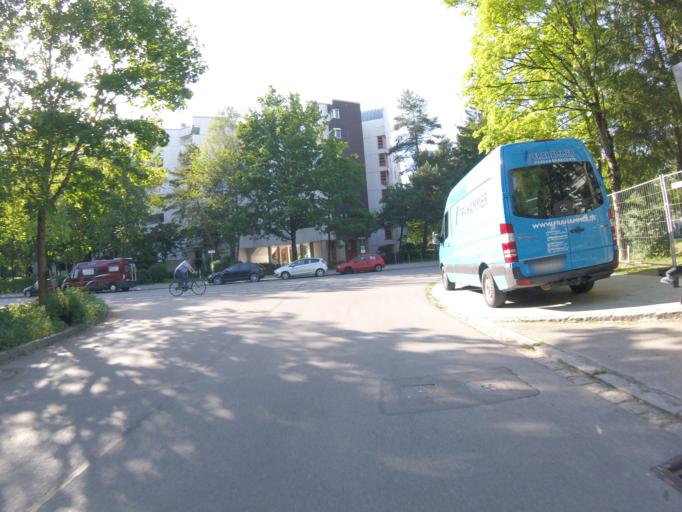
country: DE
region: Bavaria
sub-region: Upper Bavaria
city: Ottobrunn
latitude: 48.0530
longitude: 11.6643
